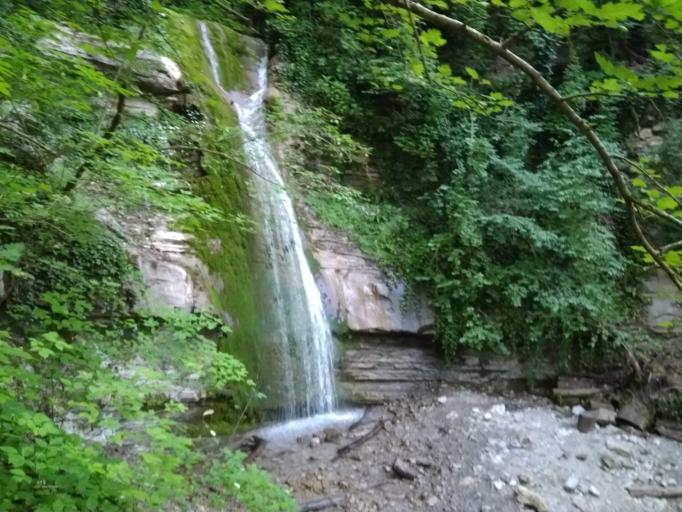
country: RU
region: Krasnodarskiy
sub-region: Sochi City
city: Lazarevskoye
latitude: 43.9984
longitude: 39.3970
